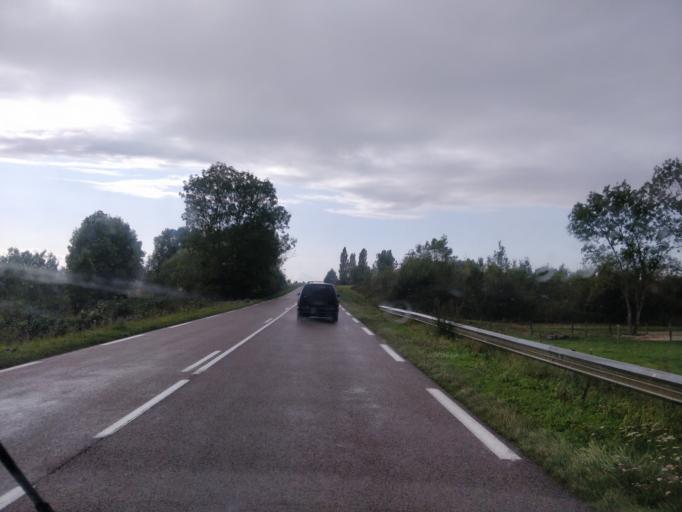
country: FR
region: Champagne-Ardenne
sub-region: Departement de l'Aube
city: Lusigny-sur-Barse
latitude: 48.2429
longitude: 4.2855
